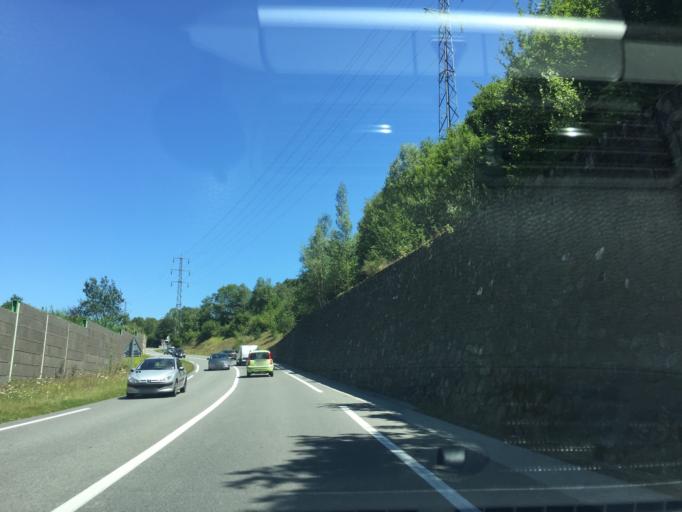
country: FR
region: Midi-Pyrenees
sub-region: Departement des Hautes-Pyrenees
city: Saint-Lary-Soulan
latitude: 42.8830
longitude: 0.3499
